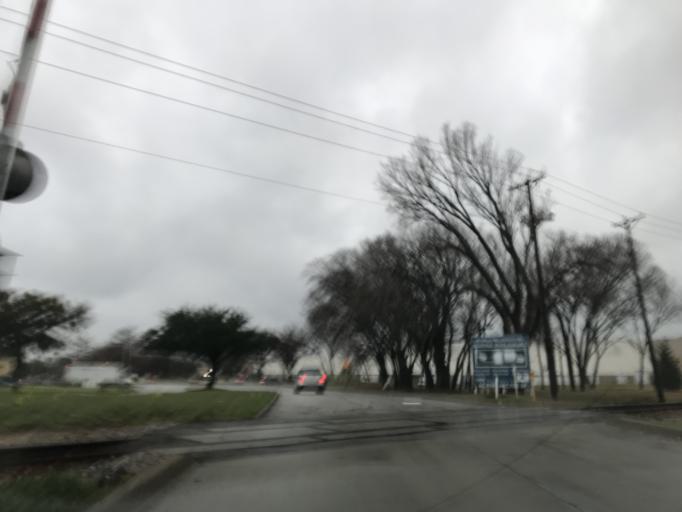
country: US
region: Texas
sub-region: Dallas County
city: Grand Prairie
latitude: 32.7721
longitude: -97.0545
